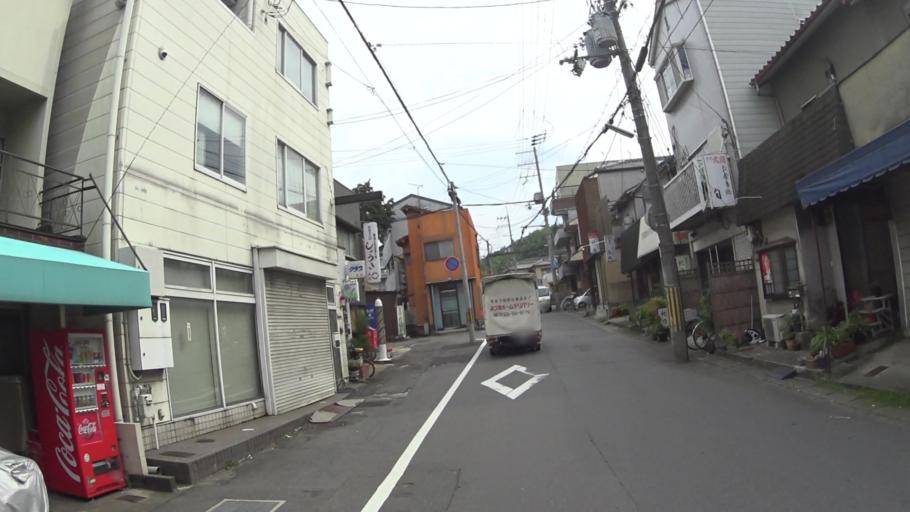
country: JP
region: Kyoto
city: Kyoto
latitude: 34.9695
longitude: 135.7993
